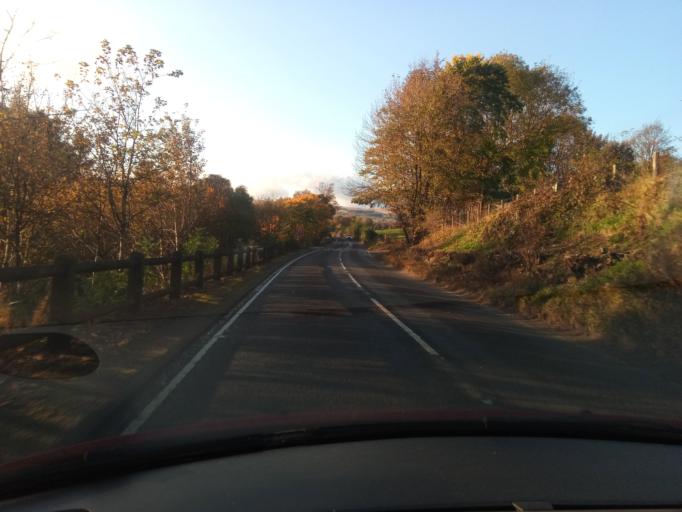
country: GB
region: England
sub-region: County Durham
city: Stanhope
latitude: 54.7362
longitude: -1.9863
